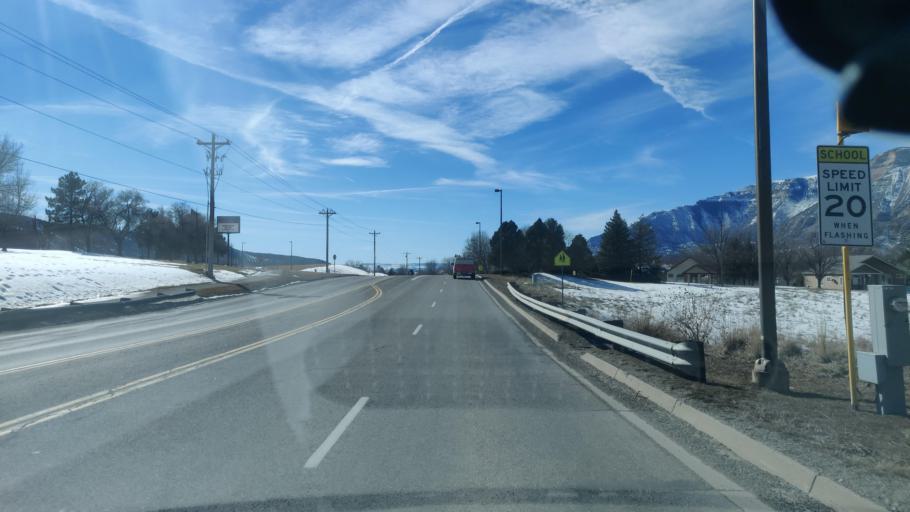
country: US
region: Colorado
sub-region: Garfield County
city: Battlement Mesa
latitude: 39.4362
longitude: -108.0320
